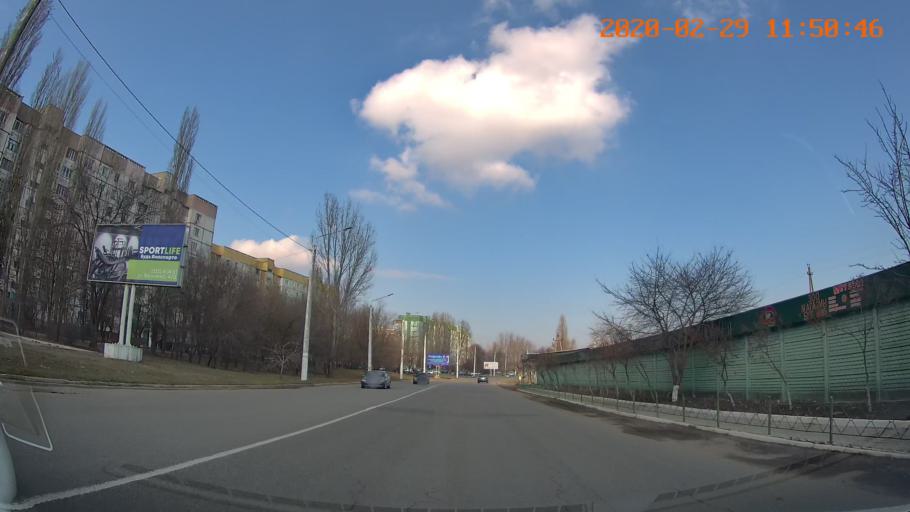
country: MD
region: Telenesti
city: Ribnita
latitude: 47.7606
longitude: 28.9898
